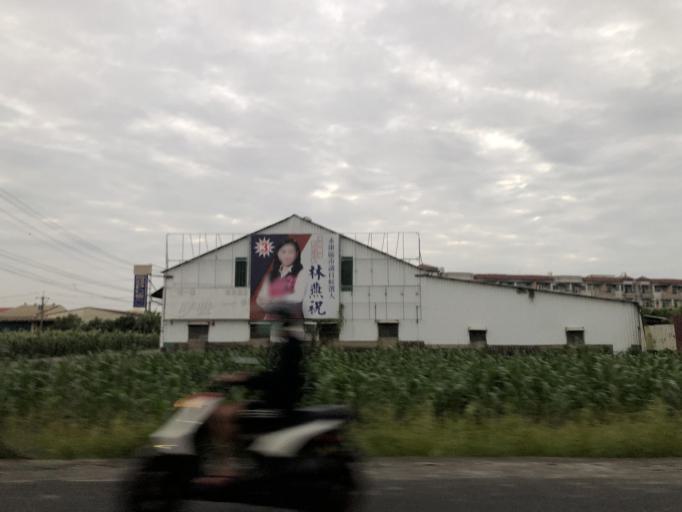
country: TW
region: Taiwan
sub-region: Tainan
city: Tainan
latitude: 23.0209
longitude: 120.2656
